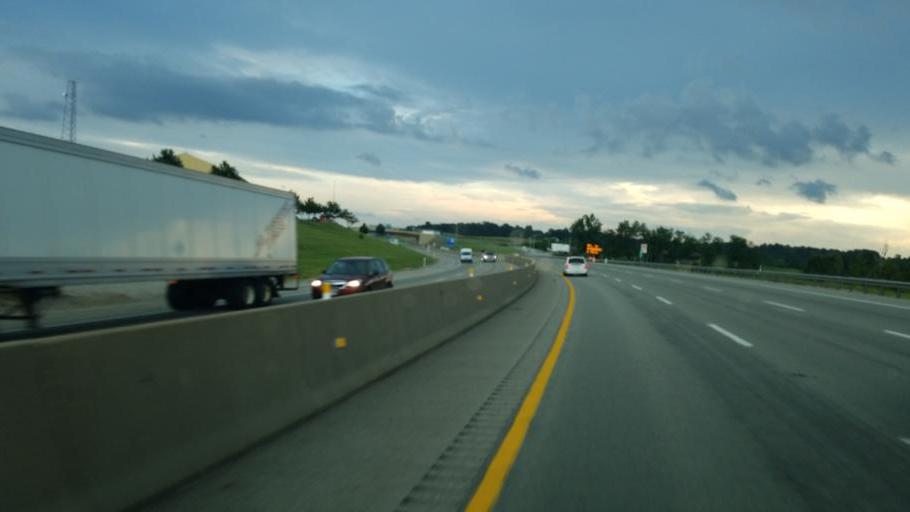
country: US
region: Pennsylvania
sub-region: Fayette County
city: Bear Rocks
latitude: 40.1290
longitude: -79.4080
